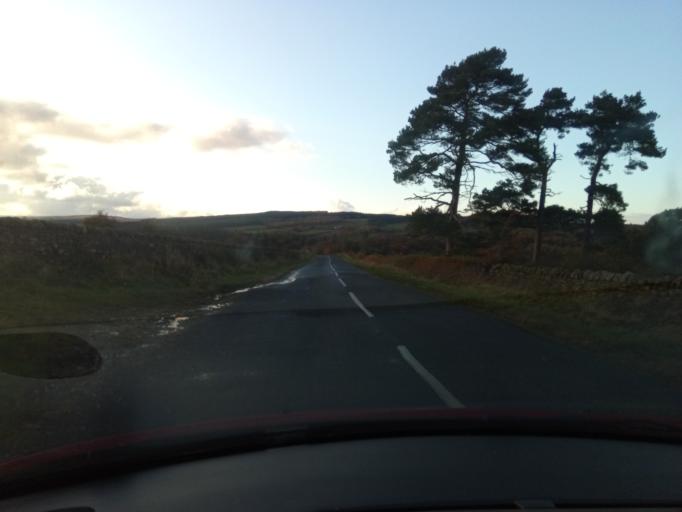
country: GB
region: England
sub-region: County Durham
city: Hamsterley
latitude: 54.6780
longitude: -1.8359
